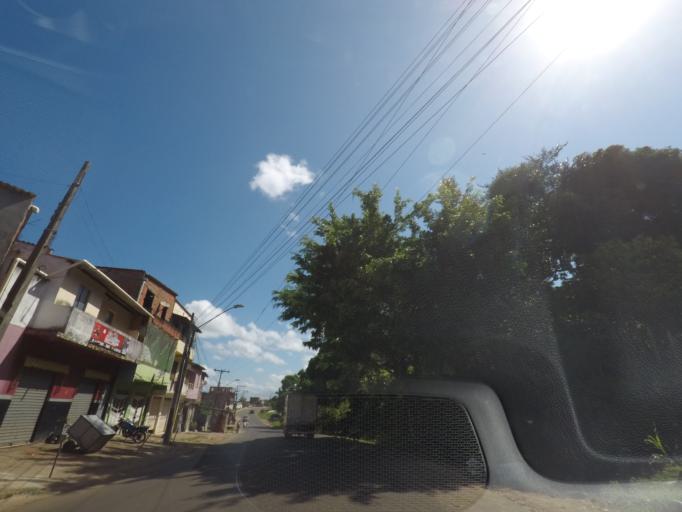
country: BR
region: Bahia
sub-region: Itubera
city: Itubera
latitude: -13.7428
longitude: -39.1510
